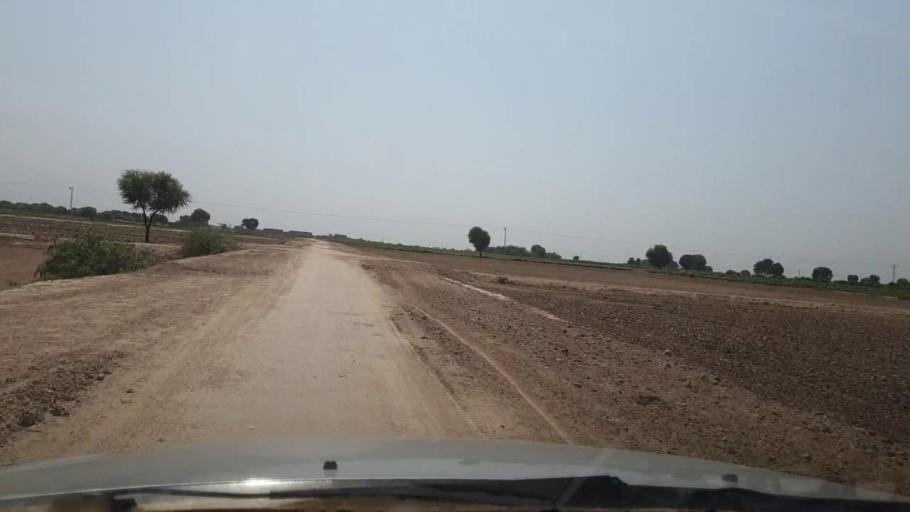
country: PK
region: Sindh
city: Chambar
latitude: 25.2657
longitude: 68.7576
